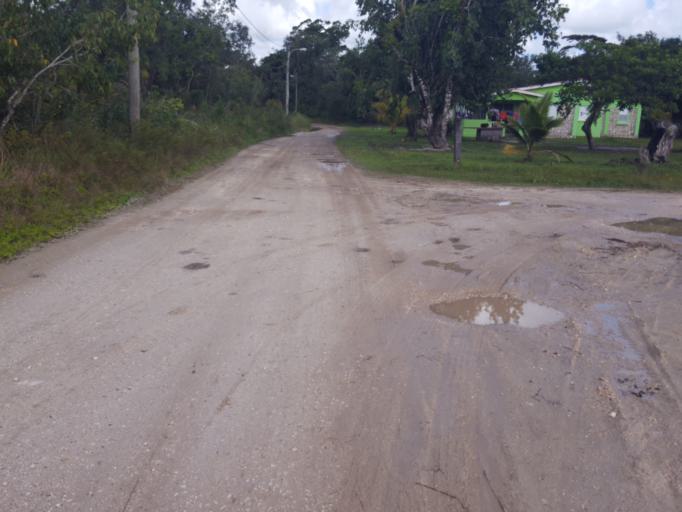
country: BZ
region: Belize
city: Belize City
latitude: 17.5707
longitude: -88.4086
